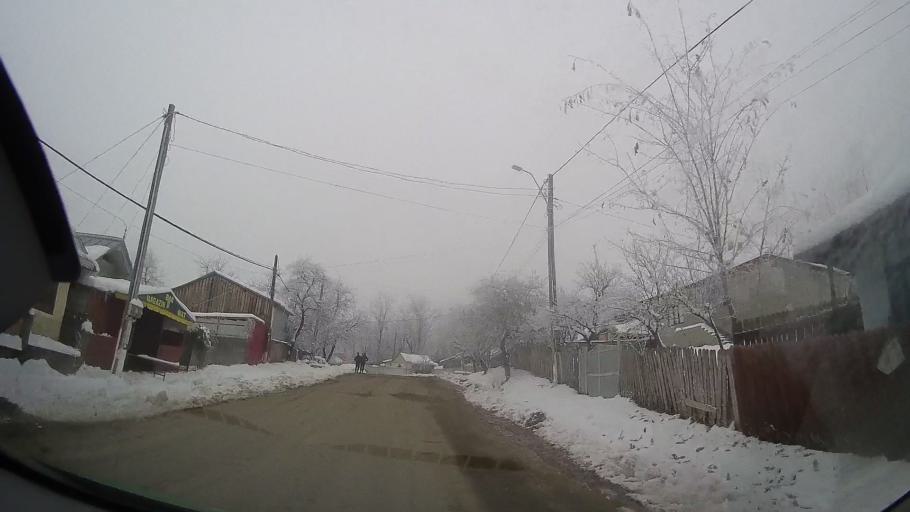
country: RO
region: Iasi
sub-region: Comuna Tansa
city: Tansa
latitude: 46.9072
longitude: 27.2417
